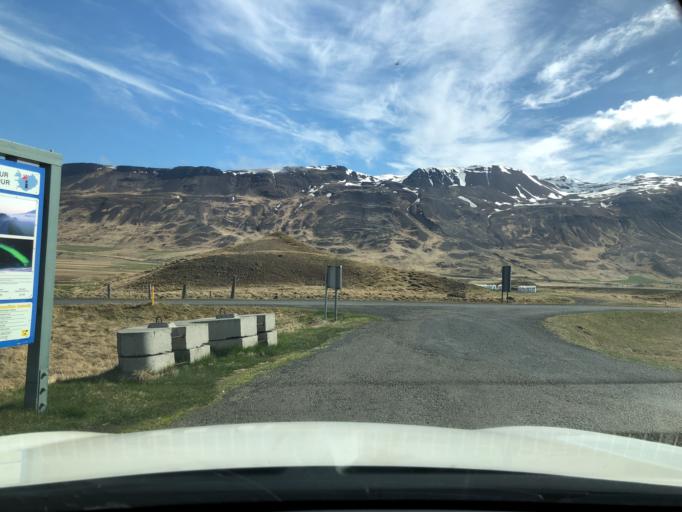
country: IS
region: Northwest
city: Saudarkrokur
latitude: 65.5045
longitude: -20.3767
